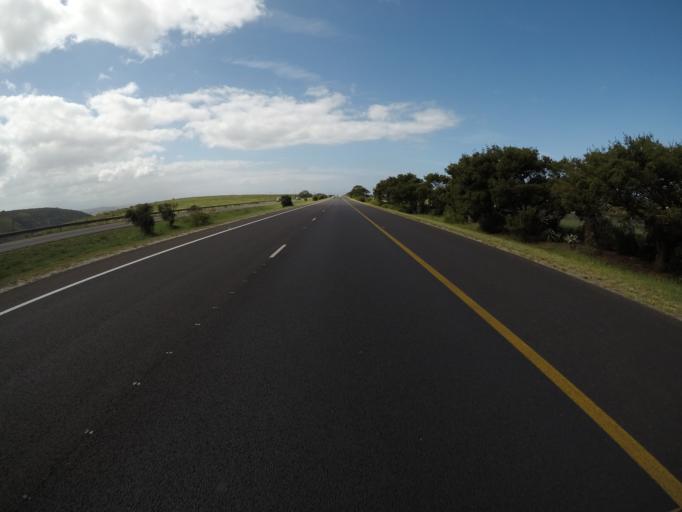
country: ZA
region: Western Cape
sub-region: Eden District Municipality
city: Mossel Bay
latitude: -34.1667
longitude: 22.0839
